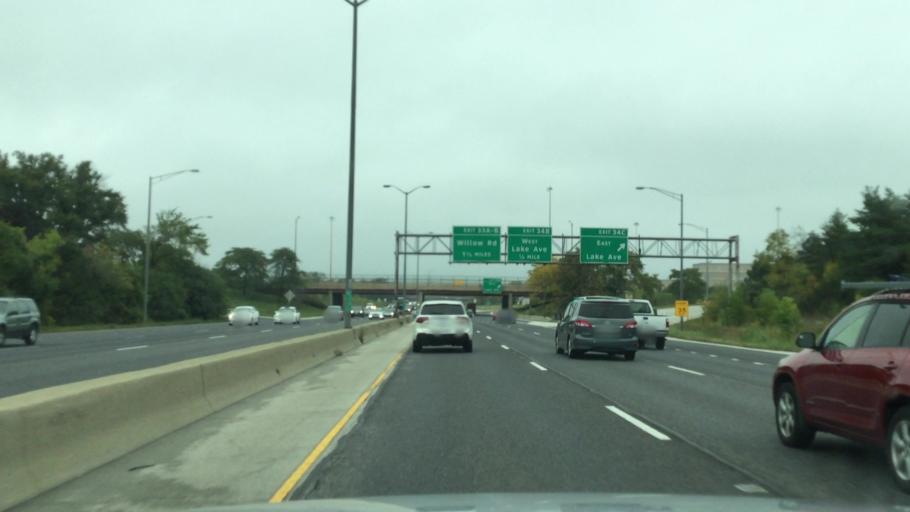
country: US
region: Illinois
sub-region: Cook County
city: Glenview
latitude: 42.0777
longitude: -87.7586
